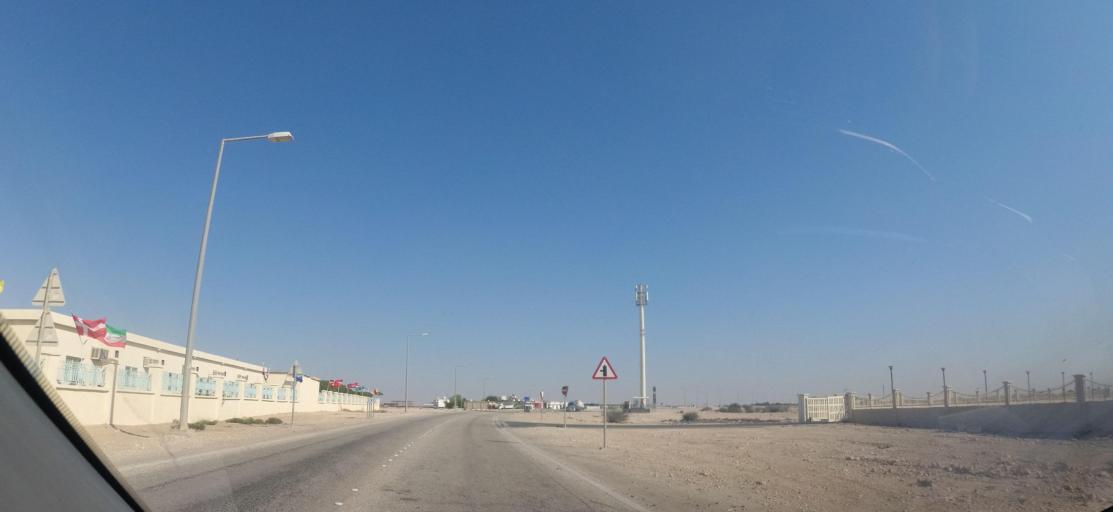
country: QA
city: Al Jumayliyah
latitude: 25.6182
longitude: 51.0820
